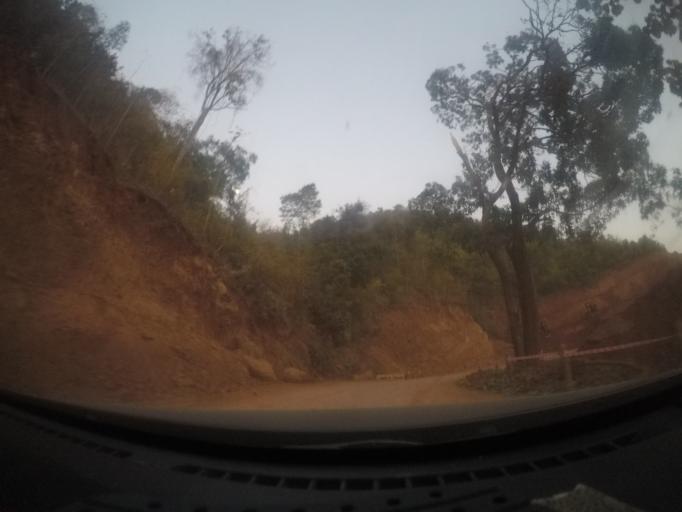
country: MM
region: Mandalay
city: Yamethin
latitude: 20.7066
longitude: 96.5030
